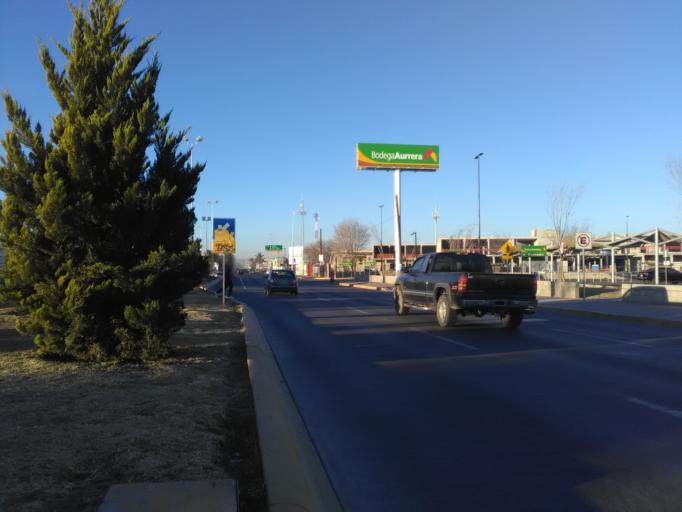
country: MX
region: Durango
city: Victoria de Durango
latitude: 24.0543
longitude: -104.6425
